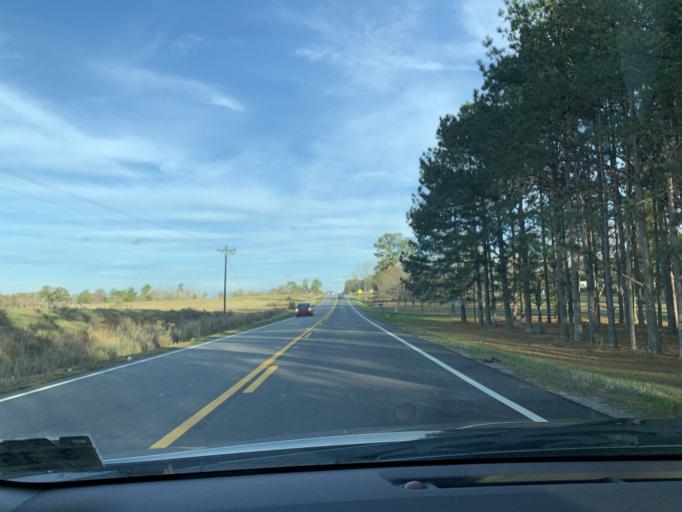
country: US
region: Georgia
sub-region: Irwin County
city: Ocilla
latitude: 31.5959
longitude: -83.1621
